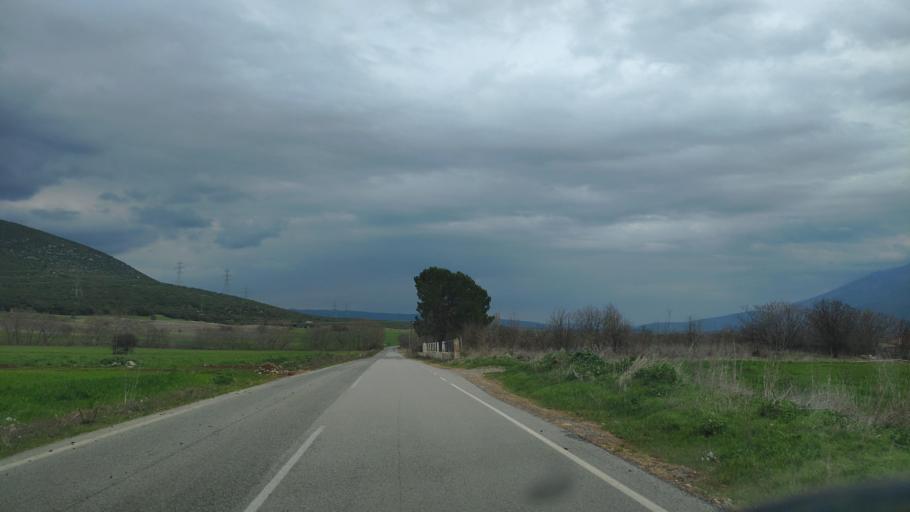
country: GR
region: Central Greece
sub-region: Nomos Fthiotidos
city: Amfikleia
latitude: 38.7072
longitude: 22.4970
